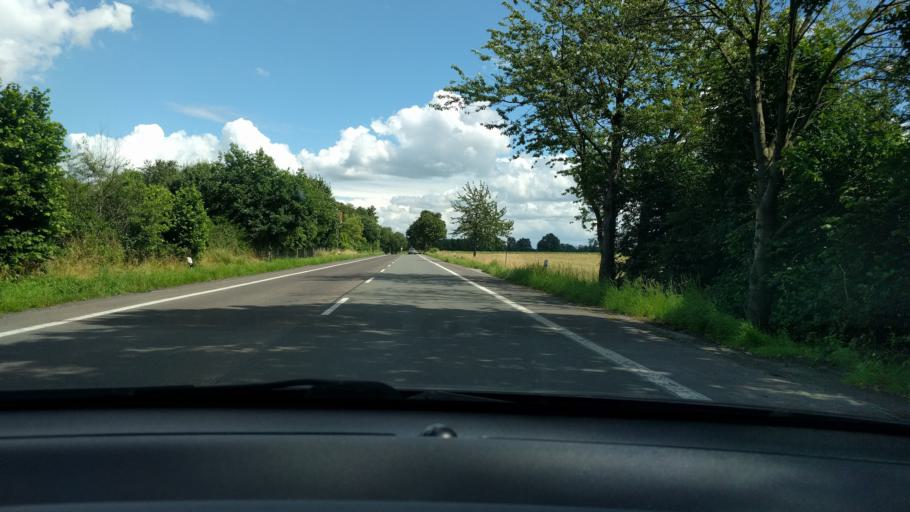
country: DE
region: North Rhine-Westphalia
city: Olfen
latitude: 51.6883
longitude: 7.3192
